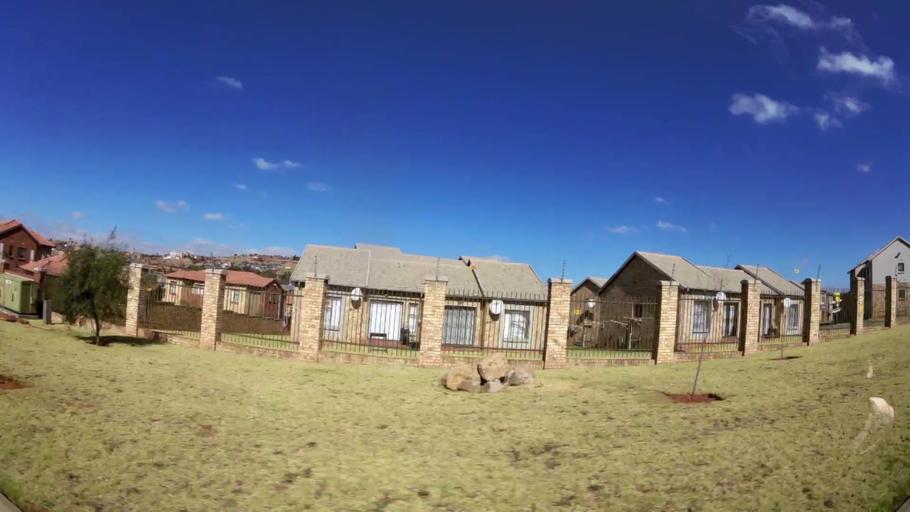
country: ZA
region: Gauteng
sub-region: West Rand District Municipality
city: Krugersdorp
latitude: -26.0837
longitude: 27.8136
